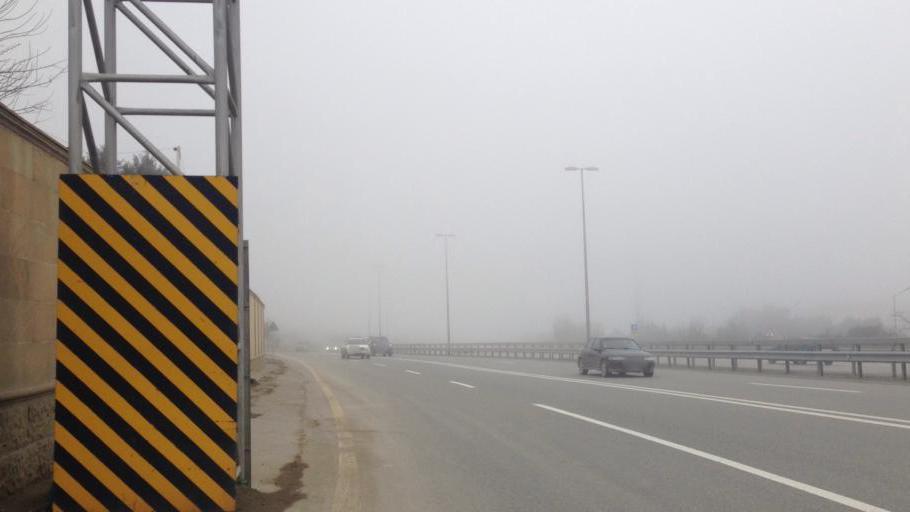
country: AZ
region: Baki
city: Qaracuxur
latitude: 40.3485
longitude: 49.9626
